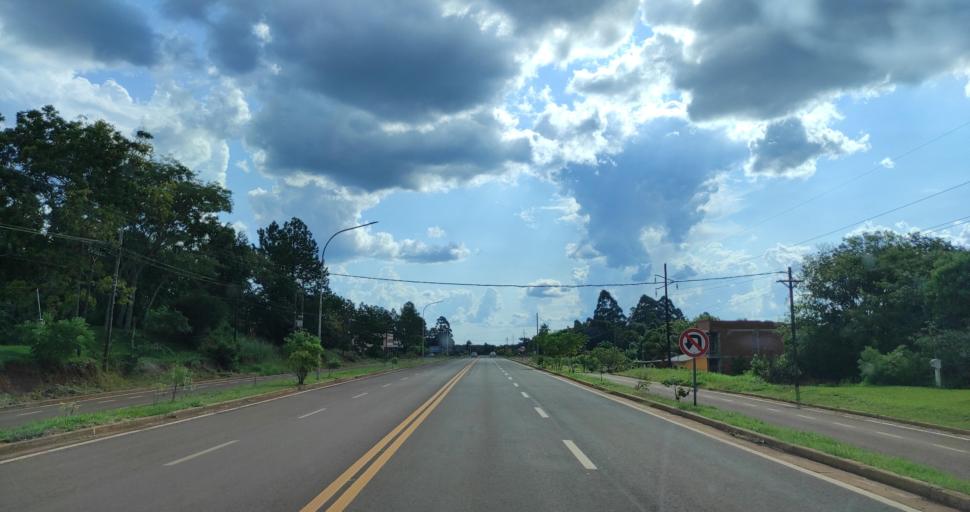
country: AR
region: Misiones
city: Bernardo de Irigoyen
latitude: -26.2935
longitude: -53.7430
